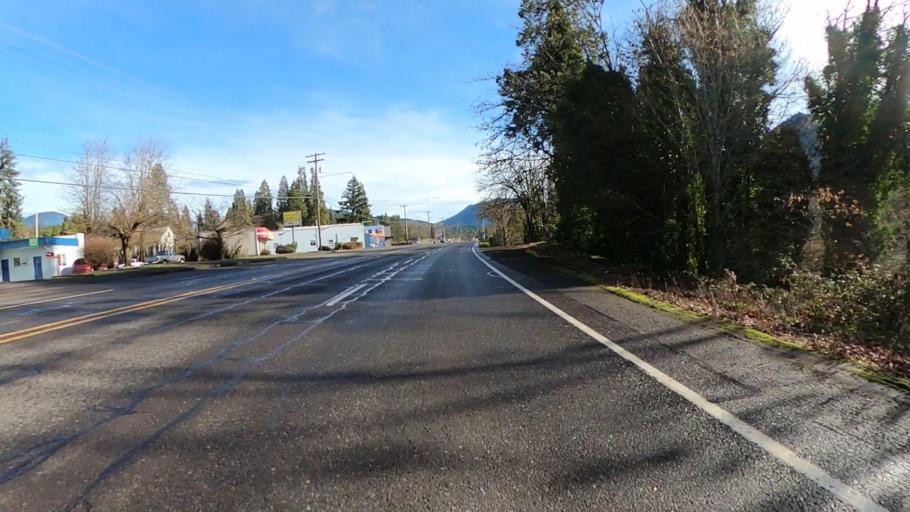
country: US
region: Oregon
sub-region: Lane County
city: Oakridge
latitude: 43.7454
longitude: -122.4697
